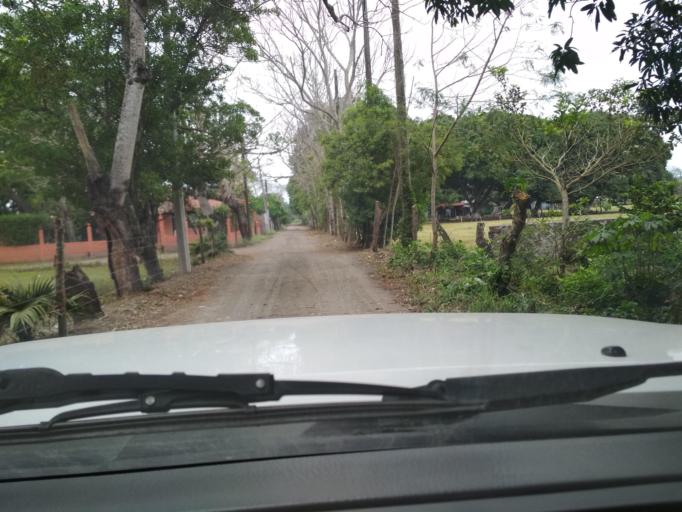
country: MX
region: Veracruz
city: Paso del Toro
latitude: 19.0526
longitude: -96.1347
